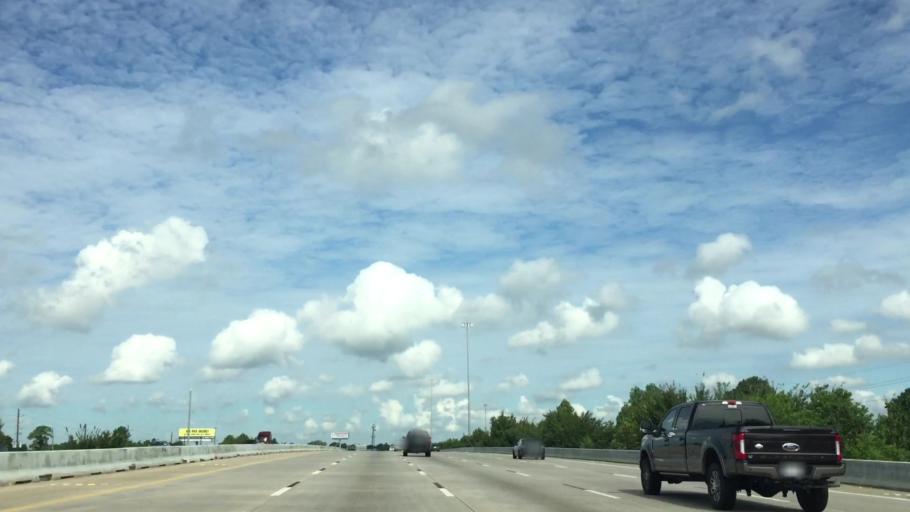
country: US
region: Texas
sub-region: Harris County
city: Jersey Village
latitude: 29.9663
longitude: -95.5551
